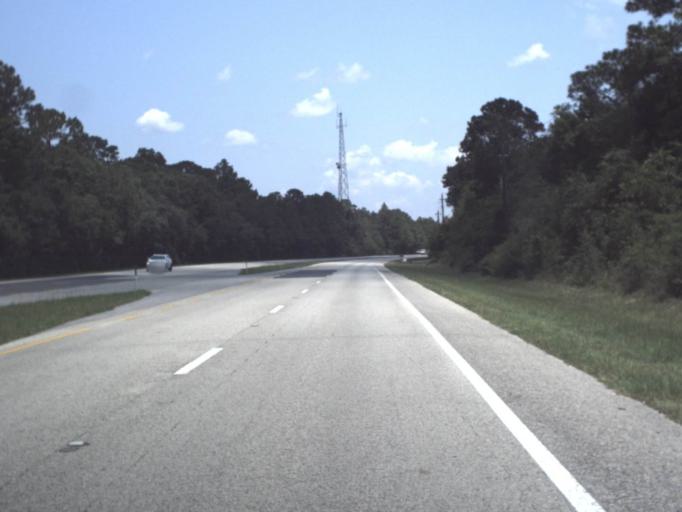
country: US
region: Florida
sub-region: Saint Johns County
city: Butler Beach
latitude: 29.6804
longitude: -81.2931
